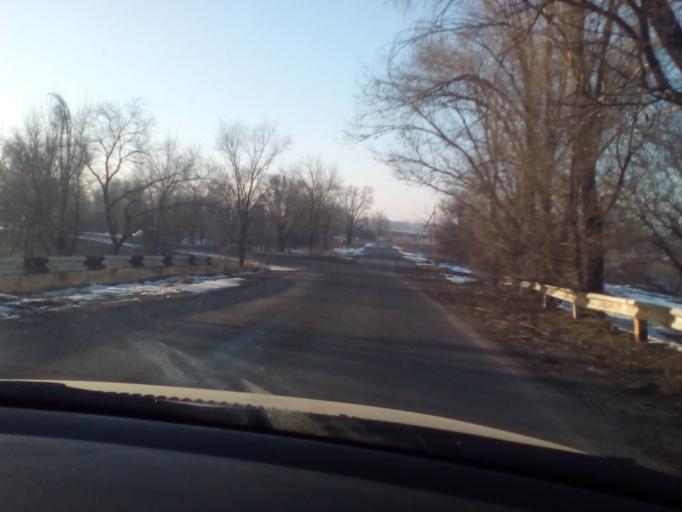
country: KZ
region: Almaty Oblysy
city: Burunday
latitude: 43.2234
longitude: 76.4104
